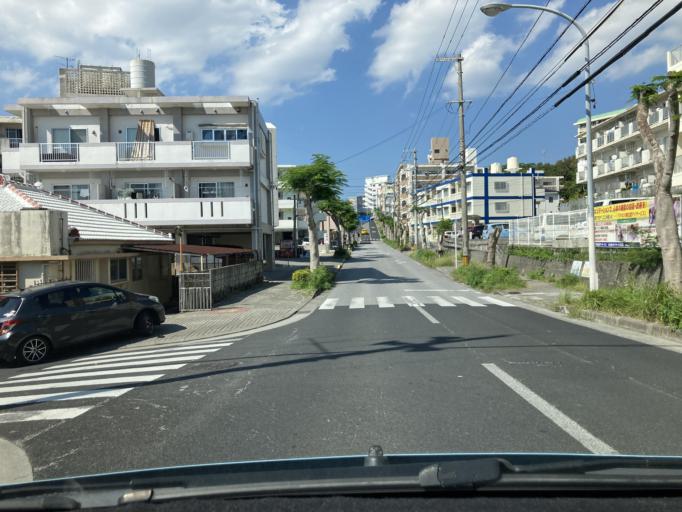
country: JP
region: Okinawa
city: Tomigusuku
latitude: 26.1981
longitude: 127.6996
